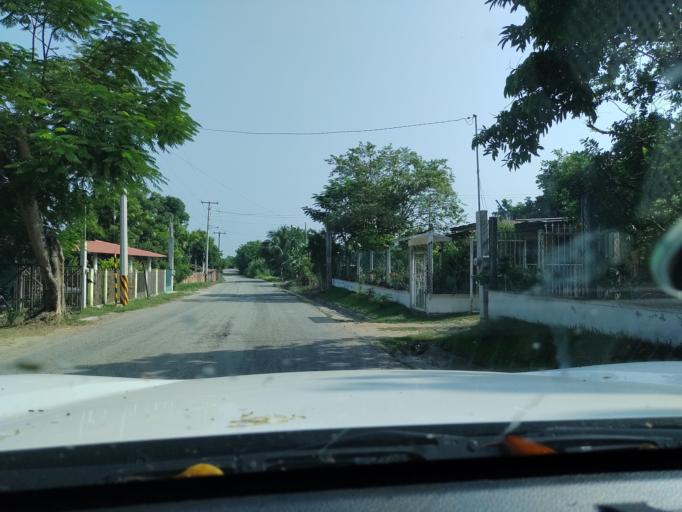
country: MX
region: Veracruz
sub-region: Martinez de la Torre
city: El Progreso
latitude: 20.0763
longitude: -97.0065
